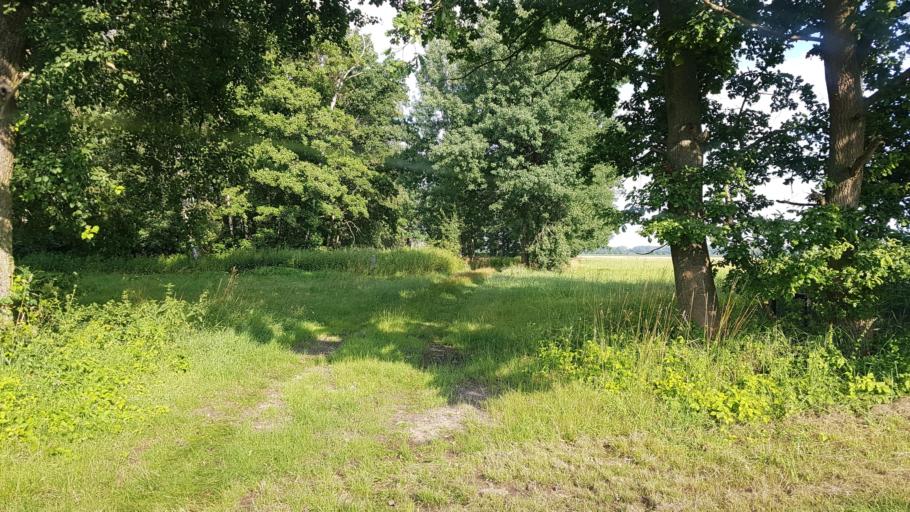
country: DE
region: Brandenburg
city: Finsterwalde
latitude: 51.6744
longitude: 13.7350
